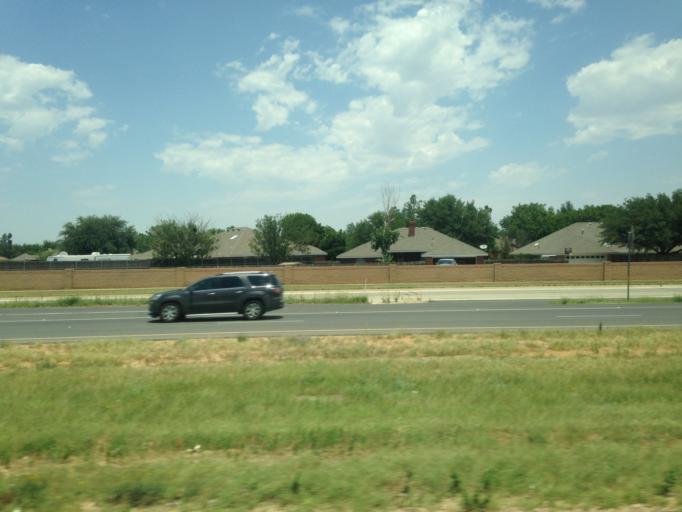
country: US
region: Texas
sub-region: Midland County
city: Midland
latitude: 32.0402
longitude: -102.1024
